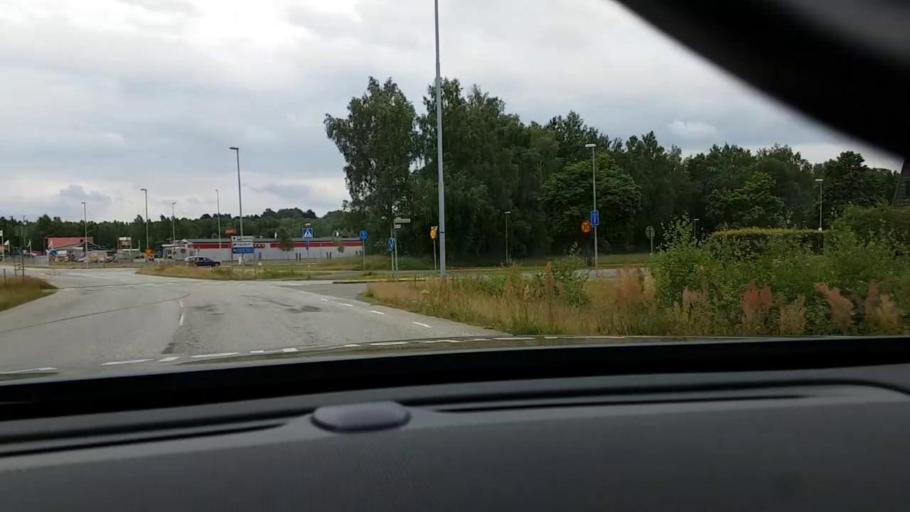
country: SE
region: Skane
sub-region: Hassleholms Kommun
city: Hassleholm
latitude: 56.1701
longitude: 13.8014
